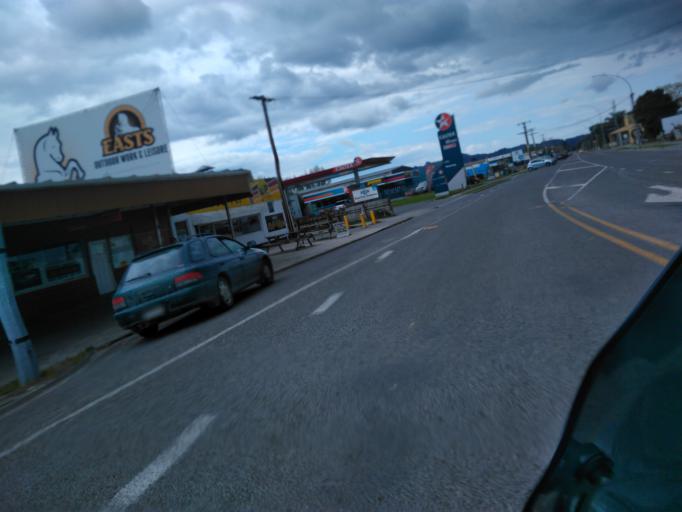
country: NZ
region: Gisborne
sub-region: Gisborne District
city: Gisborne
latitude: -38.6493
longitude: 177.9654
